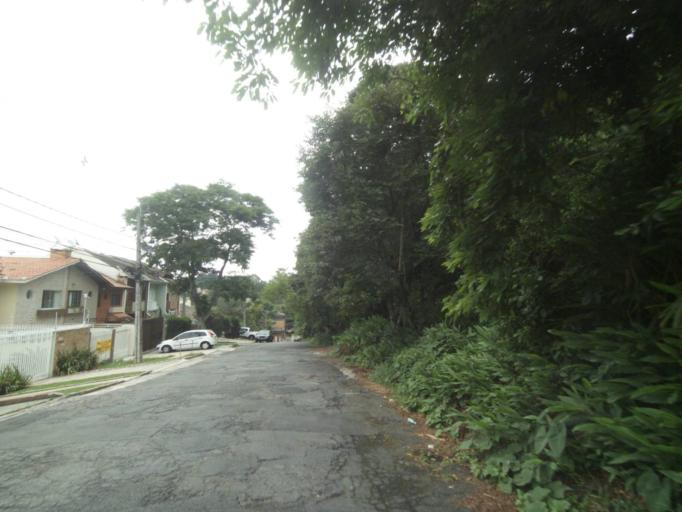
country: BR
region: Parana
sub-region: Curitiba
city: Curitiba
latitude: -25.4125
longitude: -49.3062
